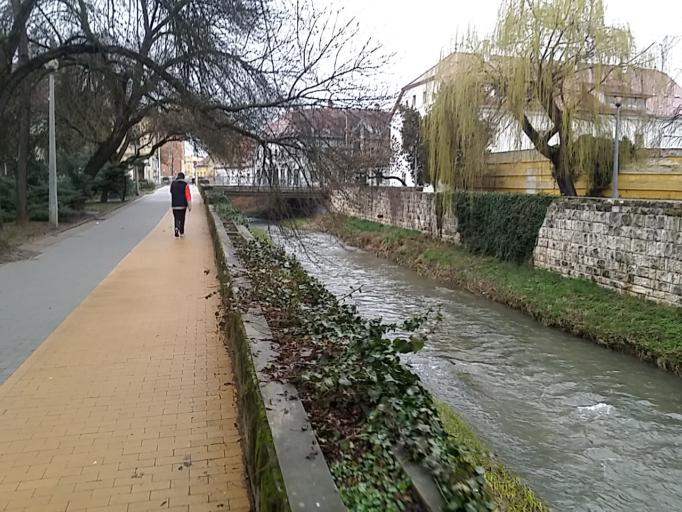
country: HU
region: Heves
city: Eger
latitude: 47.9008
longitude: 20.3802
